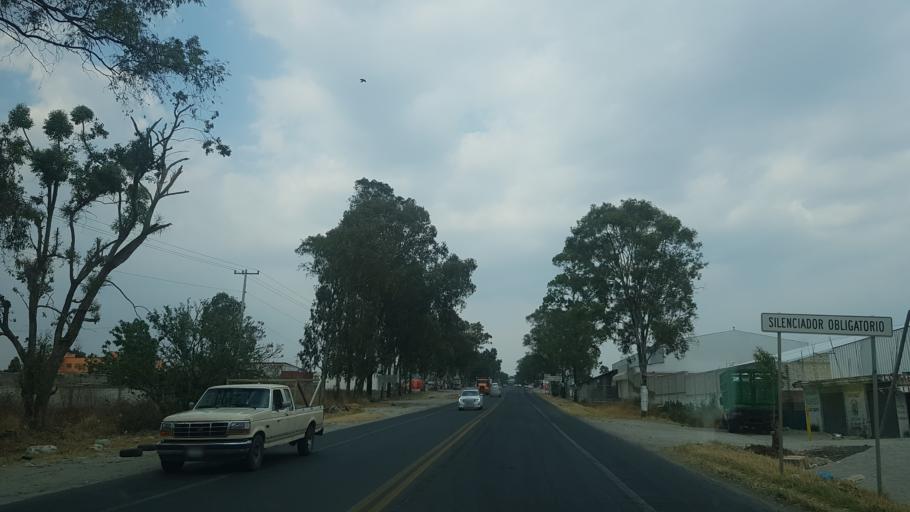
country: MX
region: Puebla
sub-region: Santa Isabel Cholula
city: San Pablo Ahuatempa
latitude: 18.9774
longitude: -98.3718
